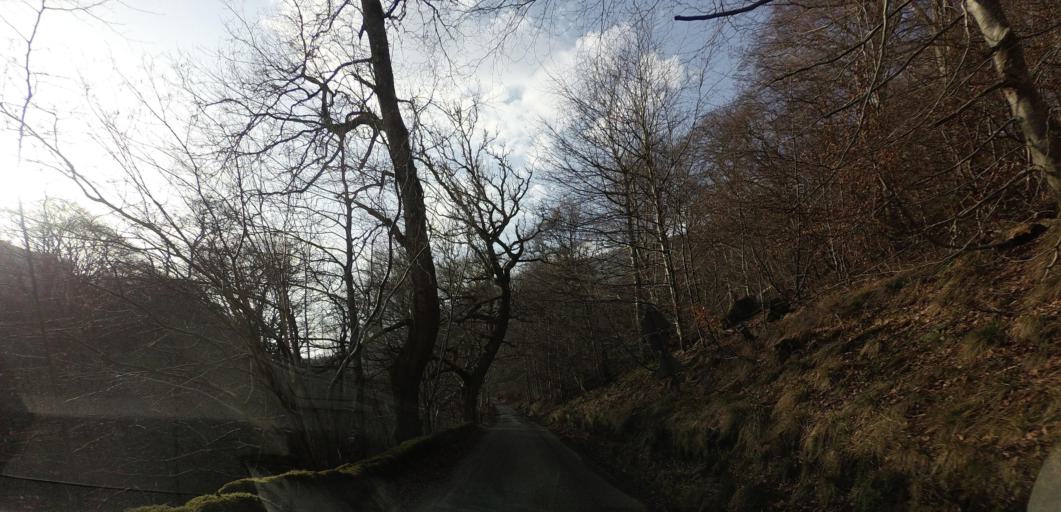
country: GB
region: Scotland
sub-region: Perth and Kinross
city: Aberfeldy
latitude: 56.6027
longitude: -4.0747
